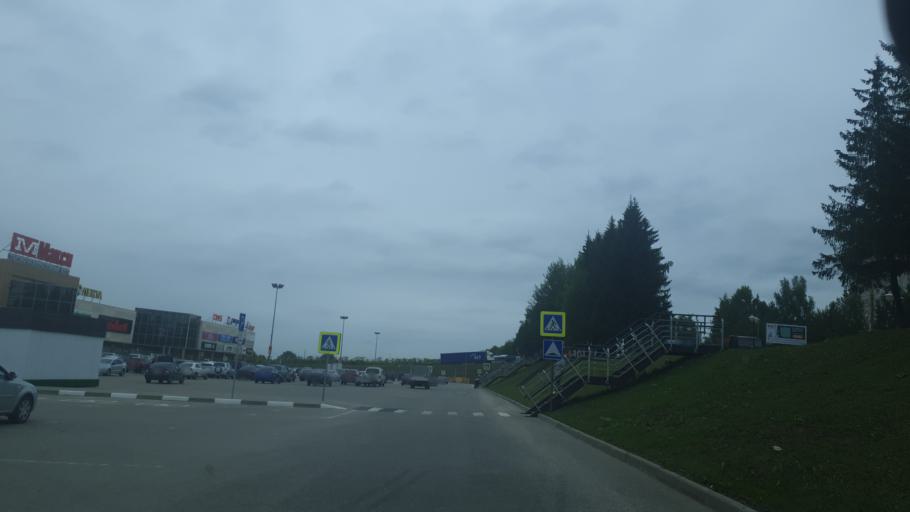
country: RU
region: Komi Republic
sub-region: Syktyvdinskiy Rayon
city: Syktyvkar
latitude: 61.6977
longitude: 50.8047
